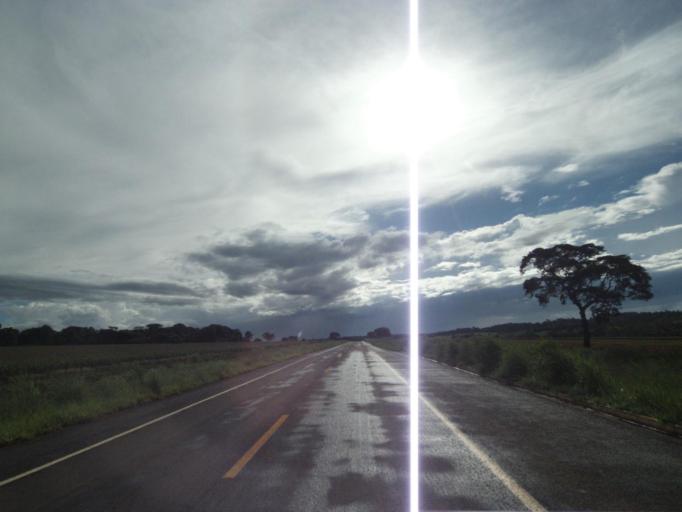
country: BR
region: Goias
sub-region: Jaragua
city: Jaragua
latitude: -15.9039
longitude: -49.5442
